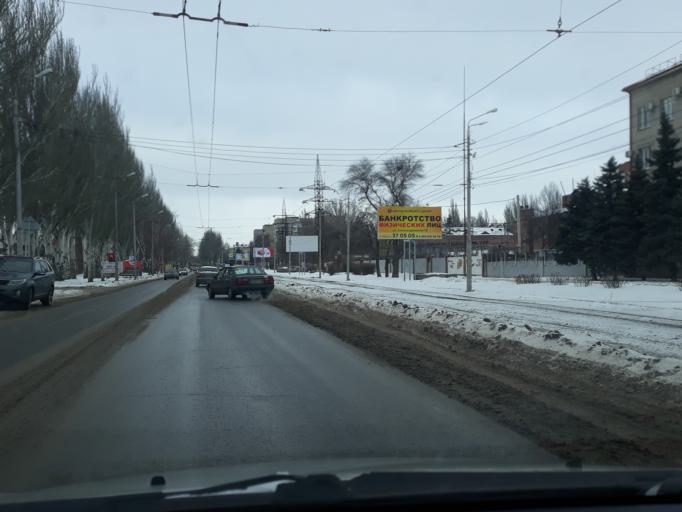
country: RU
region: Rostov
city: Taganrog
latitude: 47.2427
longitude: 38.9175
